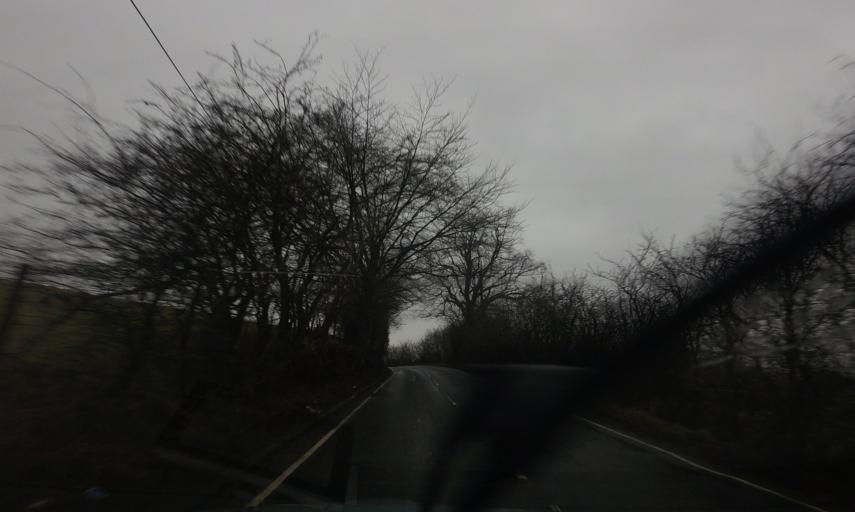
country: GB
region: Scotland
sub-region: East Dunbartonshire
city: Milngavie
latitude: 55.9574
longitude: -4.3589
